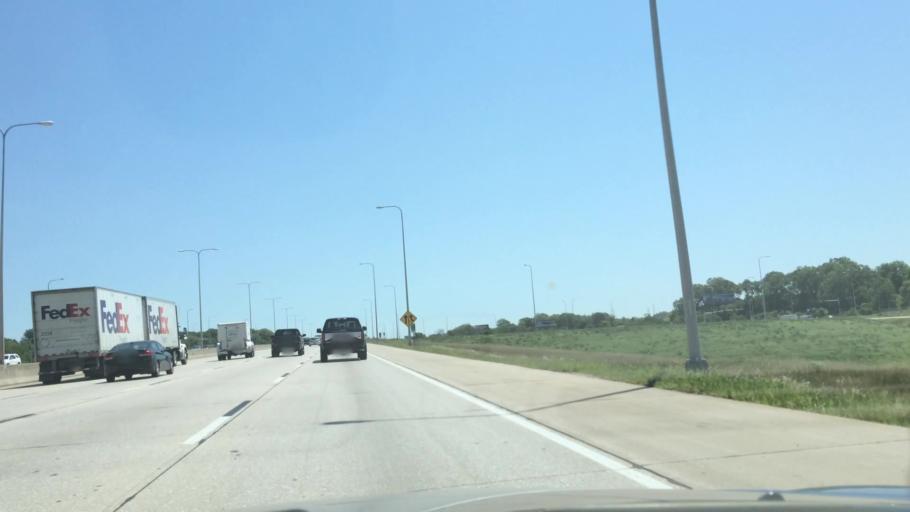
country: US
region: Nebraska
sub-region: Douglas County
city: Ralston
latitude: 41.2236
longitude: -96.0079
